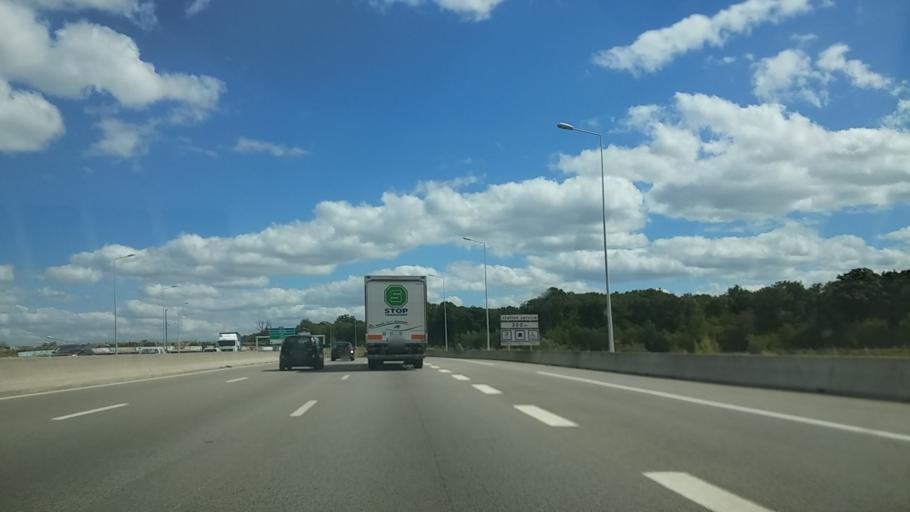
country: FR
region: Ile-de-France
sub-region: Departement des Yvelines
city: Viroflay
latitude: 48.7828
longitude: 2.1601
